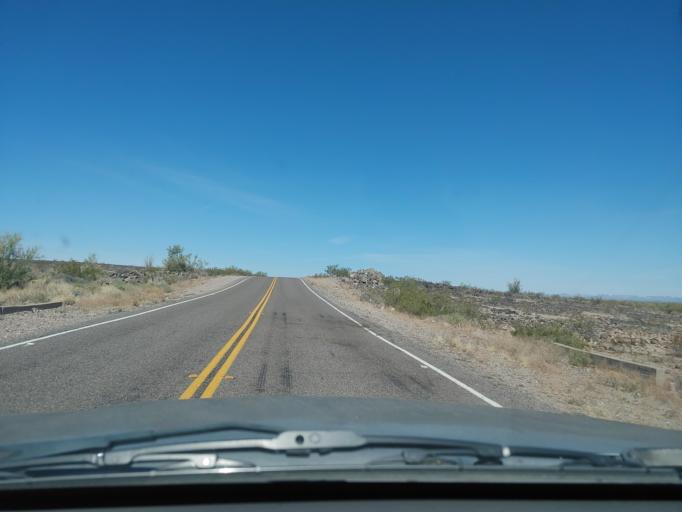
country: US
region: Arizona
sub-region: Maricopa County
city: Gila Bend
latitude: 32.8947
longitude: -113.2472
